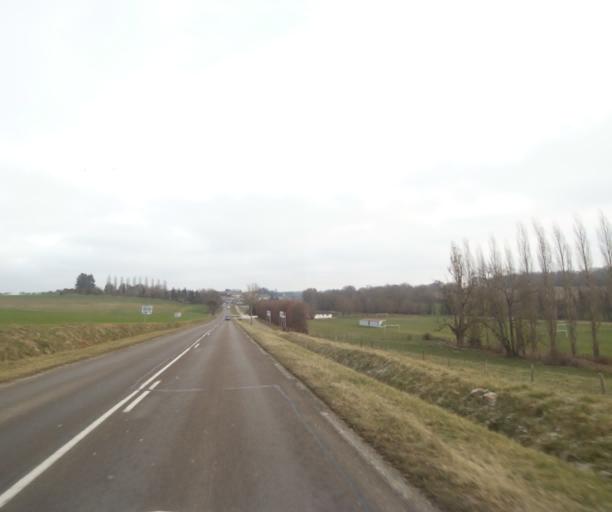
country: FR
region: Champagne-Ardenne
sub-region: Departement de la Haute-Marne
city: Chancenay
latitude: 48.6630
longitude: 4.9769
